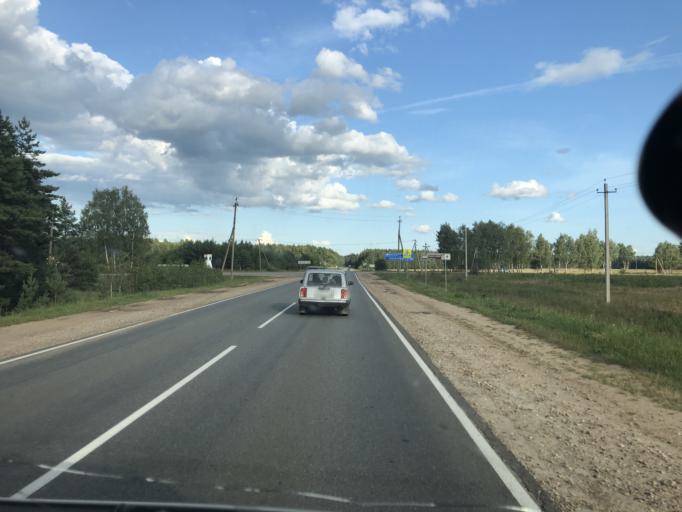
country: RU
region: Kaluga
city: Yukhnov
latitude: 54.7193
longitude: 35.2259
